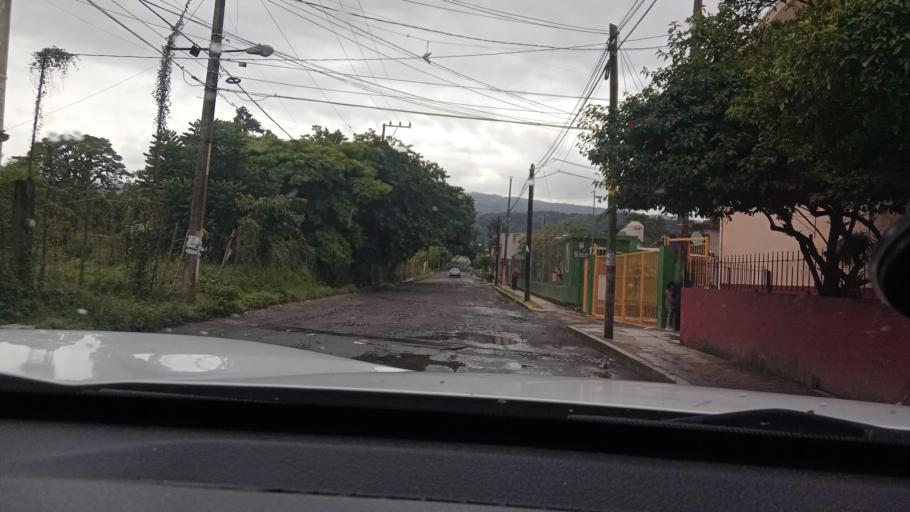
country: MX
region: Veracruz
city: Coatepec
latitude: 19.4502
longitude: -96.9730
